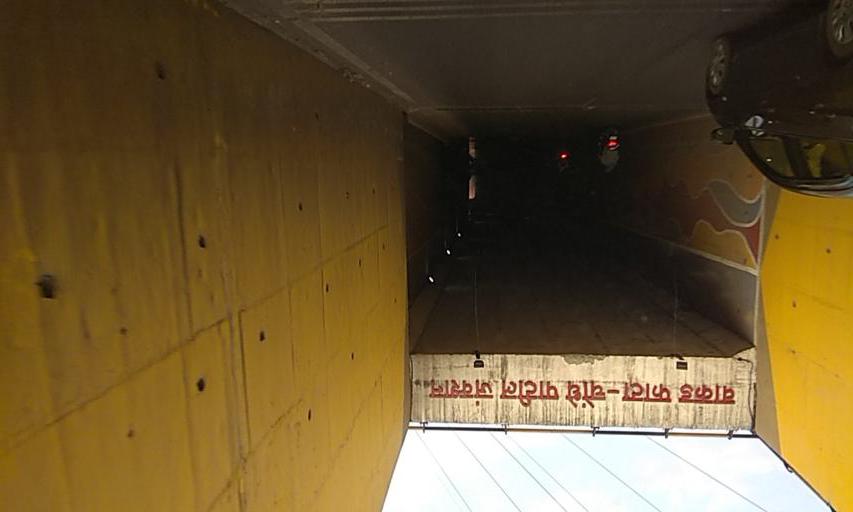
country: IN
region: Maharashtra
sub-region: Pune Division
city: Pimpri
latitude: 18.5872
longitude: 73.7889
